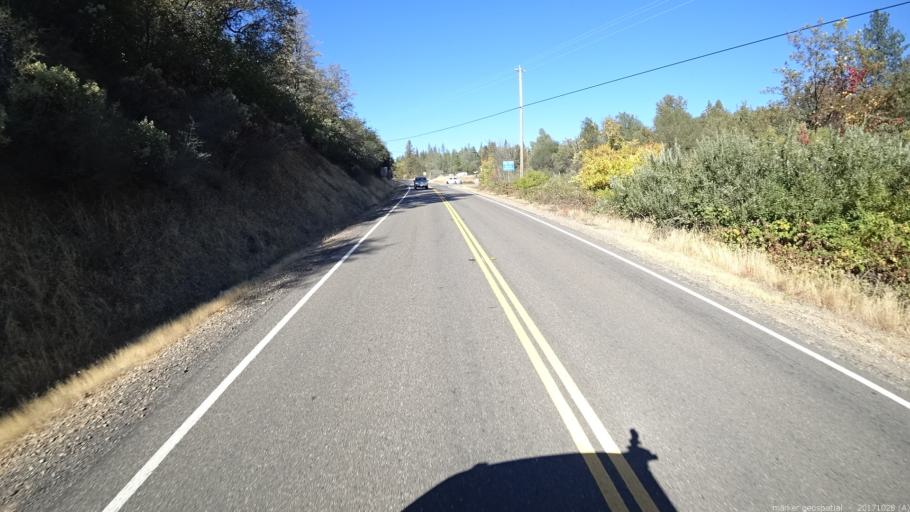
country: US
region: California
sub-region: Shasta County
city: Shasta
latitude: 40.6141
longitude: -122.4601
